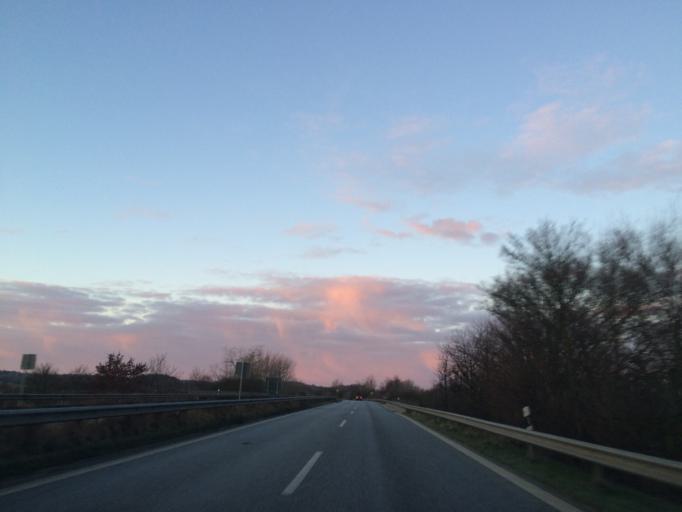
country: DE
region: Schleswig-Holstein
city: Neustadt in Holstein
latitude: 54.1243
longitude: 10.8059
